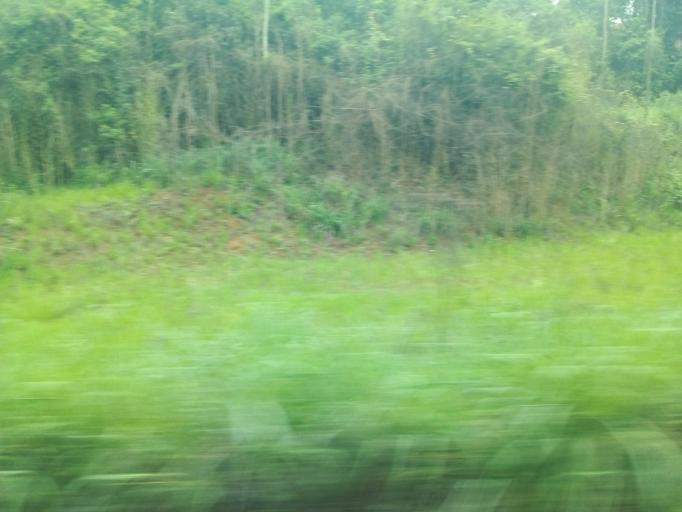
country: BR
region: Minas Gerais
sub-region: Rio Piracicaba
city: Rio Piracicaba
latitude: -19.9019
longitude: -43.1460
